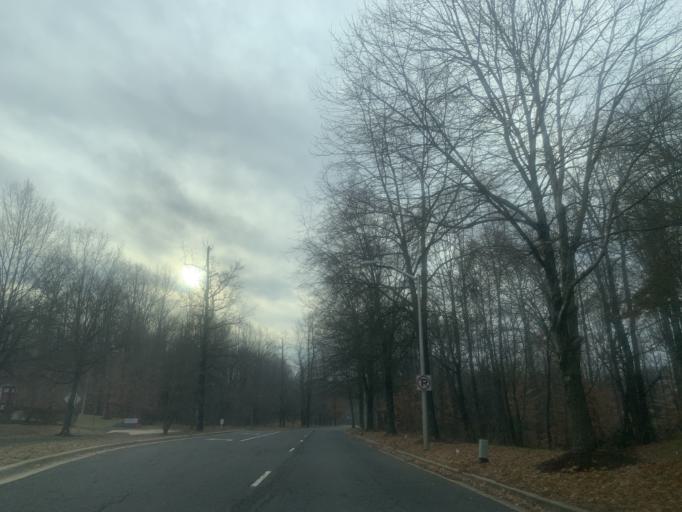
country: US
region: Maryland
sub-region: Prince George's County
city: Forestville
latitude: 38.8279
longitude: -76.8508
